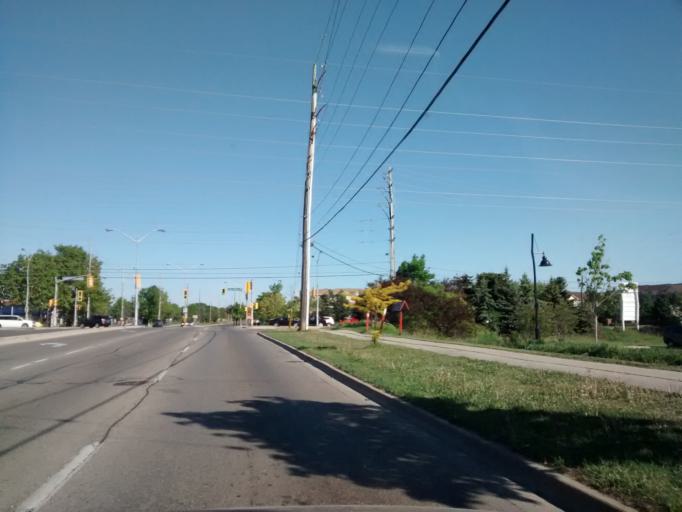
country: CA
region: Ontario
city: Burlington
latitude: 43.3788
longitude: -79.8051
